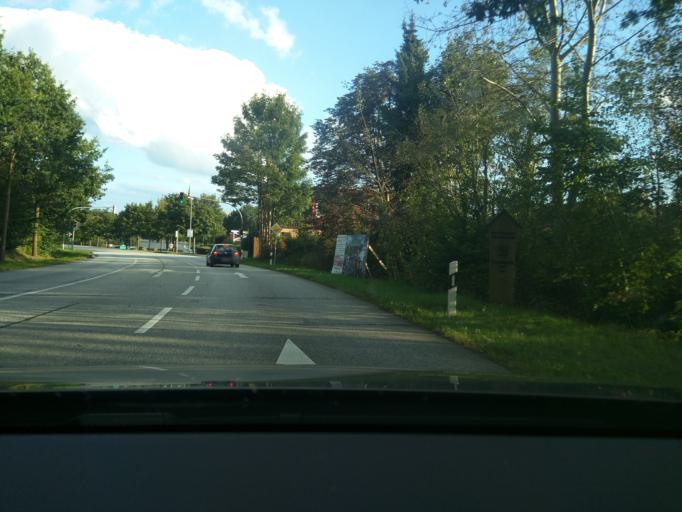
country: DE
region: Schleswig-Holstein
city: Schwarzenbek
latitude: 53.5065
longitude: 10.4749
